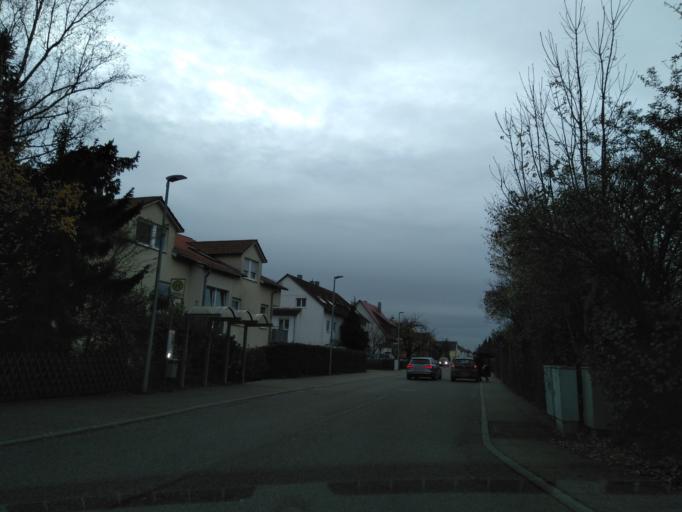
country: DE
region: Baden-Wuerttemberg
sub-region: Regierungsbezirk Stuttgart
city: Markgroningen
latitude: 48.9079
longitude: 9.0815
